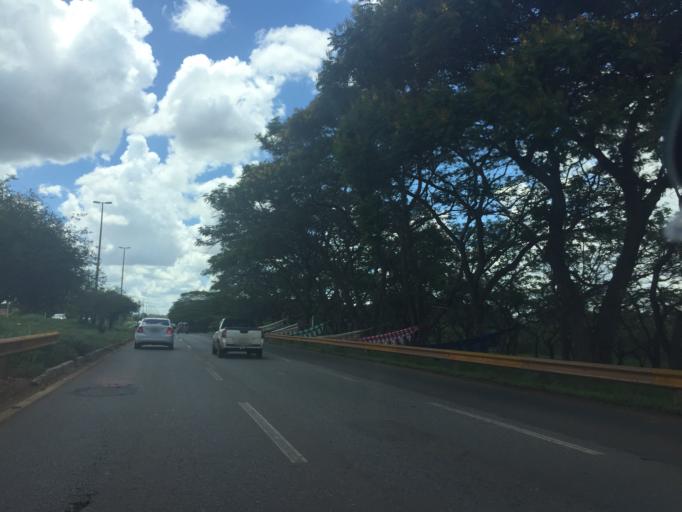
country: BR
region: Federal District
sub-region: Brasilia
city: Brasilia
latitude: -15.8658
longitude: -47.9425
